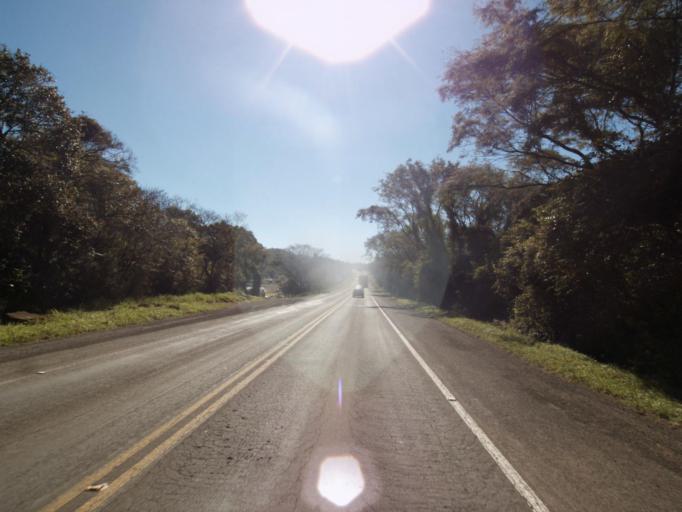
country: AR
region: Misiones
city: Bernardo de Irigoyen
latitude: -26.7903
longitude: -53.4576
